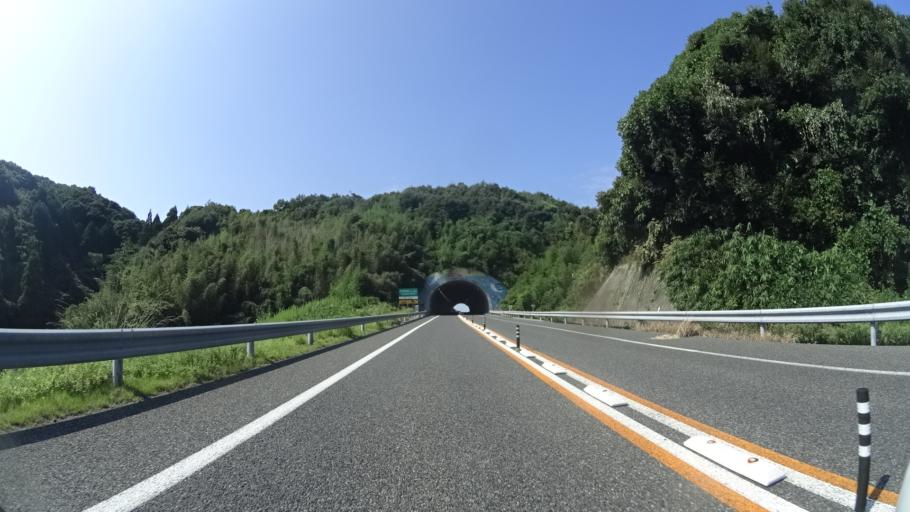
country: JP
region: Shimane
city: Gotsucho
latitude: 34.9659
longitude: 132.1669
